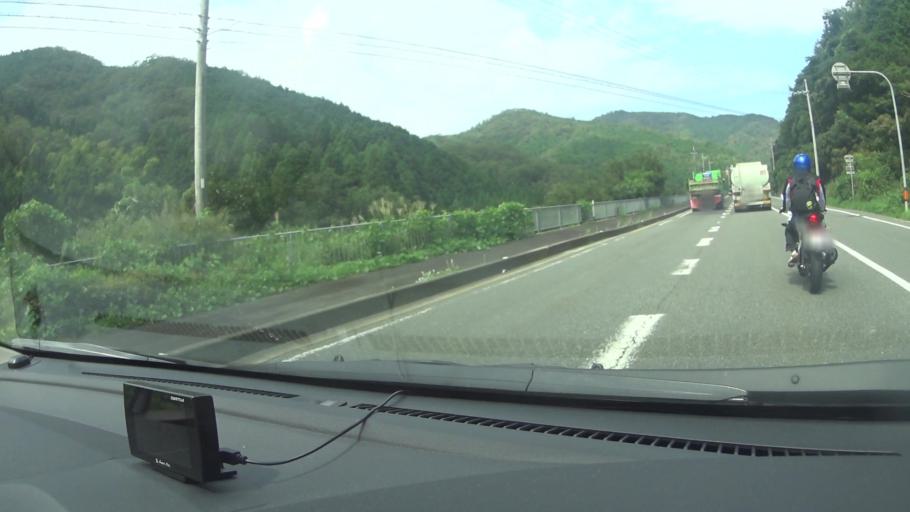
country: JP
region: Kyoto
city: Ayabe
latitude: 35.2598
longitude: 135.2750
